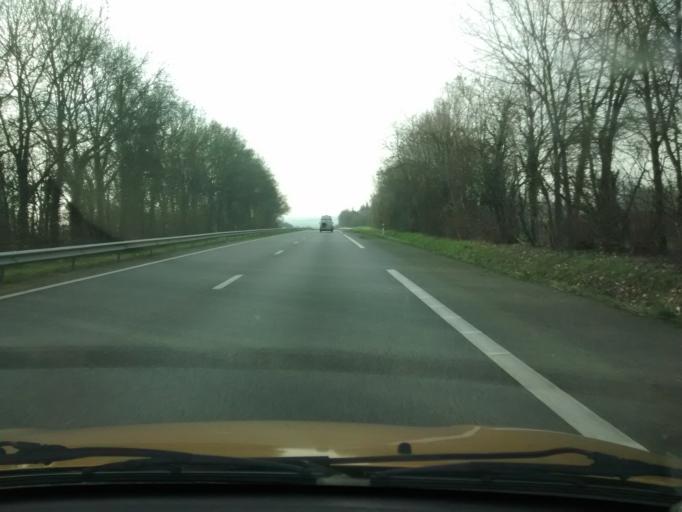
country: FR
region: Brittany
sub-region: Departement d'Ille-et-Vilaine
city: Grand-Fougeray
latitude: 47.7260
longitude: -1.7118
